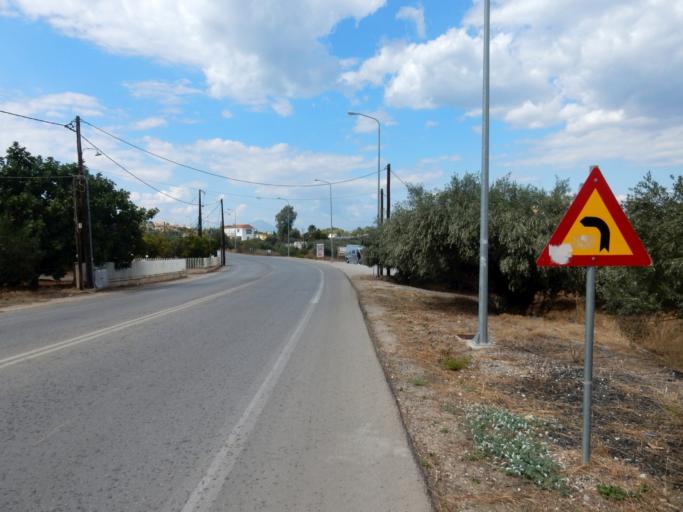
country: GR
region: Attica
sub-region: Nomarchia Anatolikis Attikis
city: Khalkoutsion
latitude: 38.3249
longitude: 23.7457
